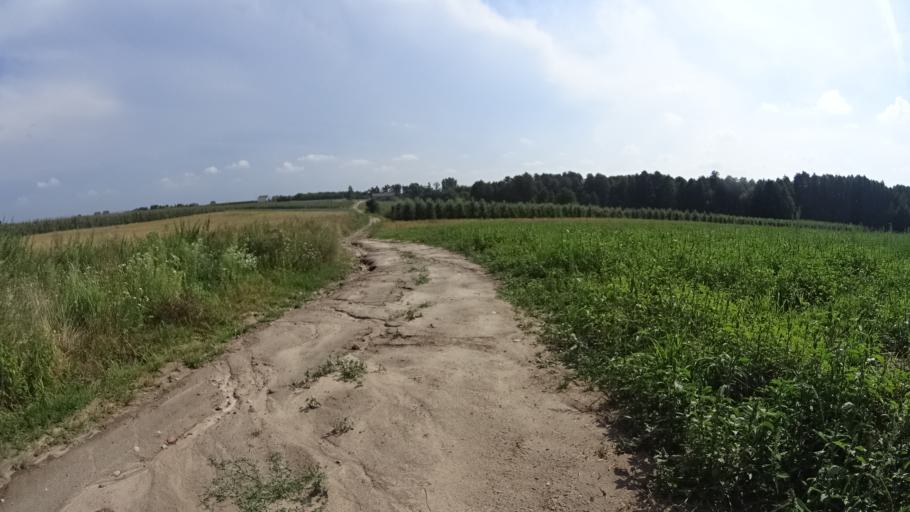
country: PL
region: Masovian Voivodeship
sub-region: Powiat grojecki
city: Goszczyn
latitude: 51.6905
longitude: 20.8390
